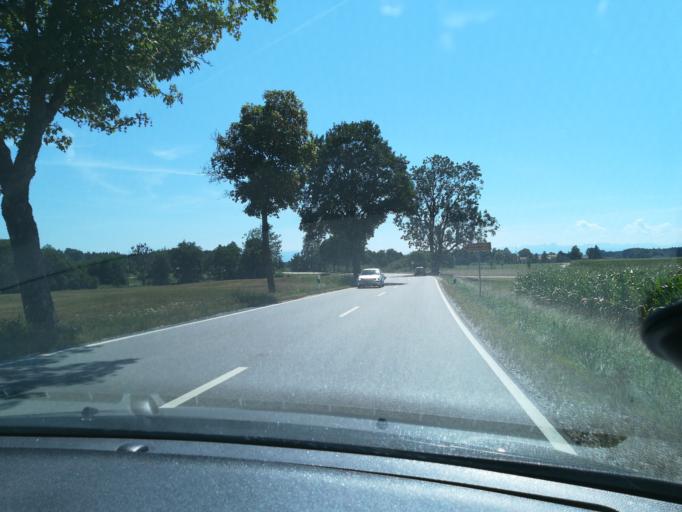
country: DE
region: Bavaria
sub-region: Upper Bavaria
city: Edling
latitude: 48.0790
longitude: 12.1611
